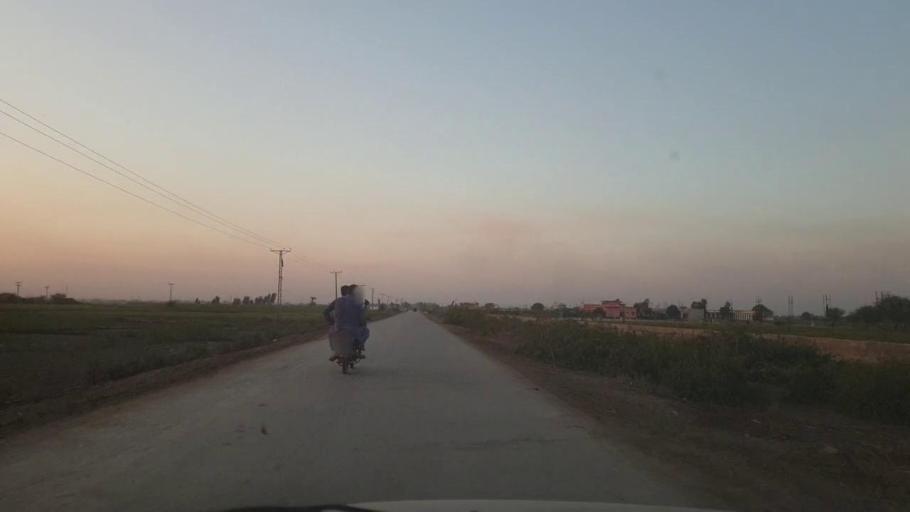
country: PK
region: Sindh
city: Mirpur Khas
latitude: 25.4920
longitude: 69.0394
